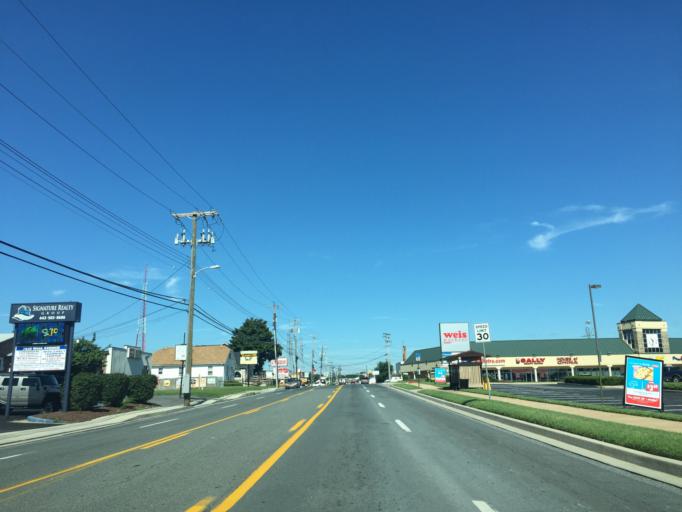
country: US
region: Maryland
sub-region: Baltimore County
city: Dundalk
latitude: 39.2670
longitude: -76.4961
